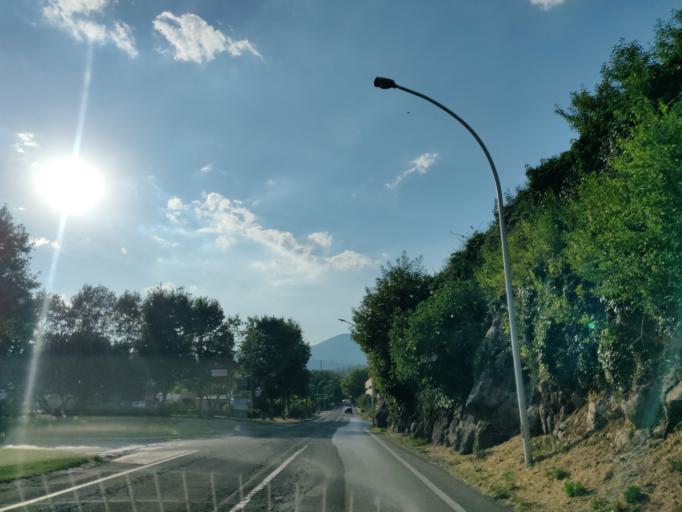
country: IT
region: Tuscany
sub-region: Provincia di Siena
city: Piancastagnaio
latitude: 42.8517
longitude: 11.6884
